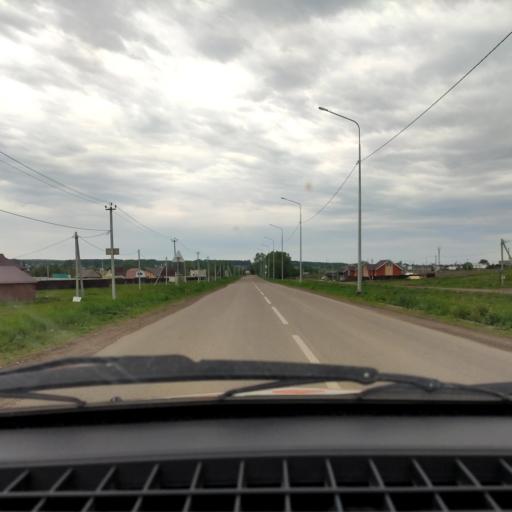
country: RU
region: Bashkortostan
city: Avdon
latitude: 54.5547
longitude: 55.7599
